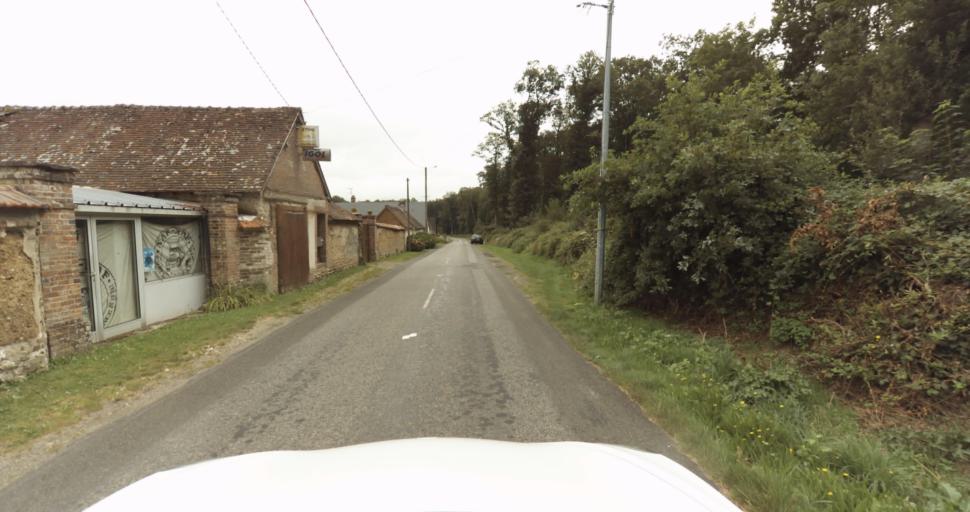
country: FR
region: Haute-Normandie
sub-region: Departement de l'Eure
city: Arnieres-sur-Iton
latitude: 48.9537
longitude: 1.0677
